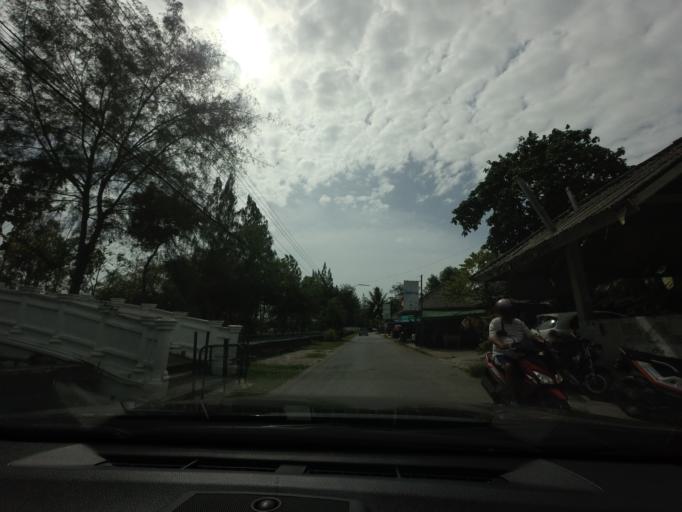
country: TH
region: Pattani
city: Pattani
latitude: 6.8943
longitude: 101.2468
